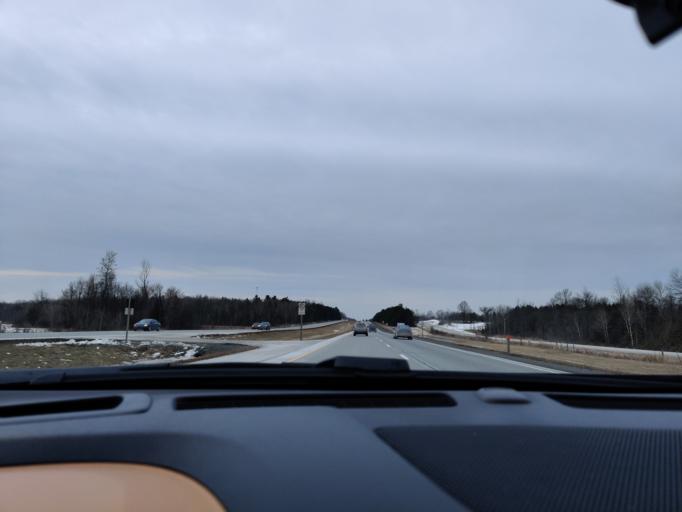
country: US
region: New York
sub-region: St. Lawrence County
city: Ogdensburg
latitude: 44.8073
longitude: -75.4111
